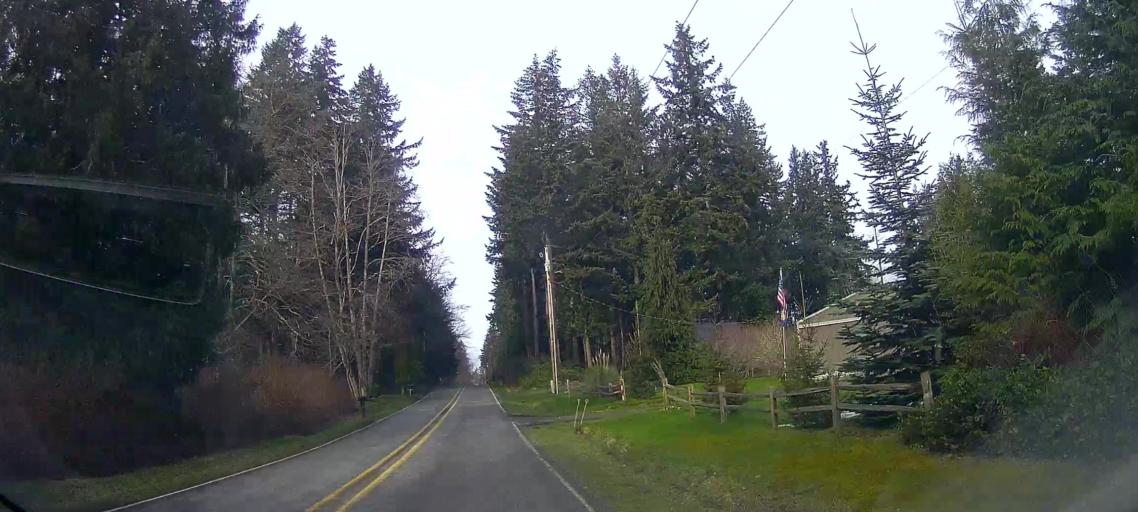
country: US
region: Washington
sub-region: Island County
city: Langley
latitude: 48.0732
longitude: -122.3721
